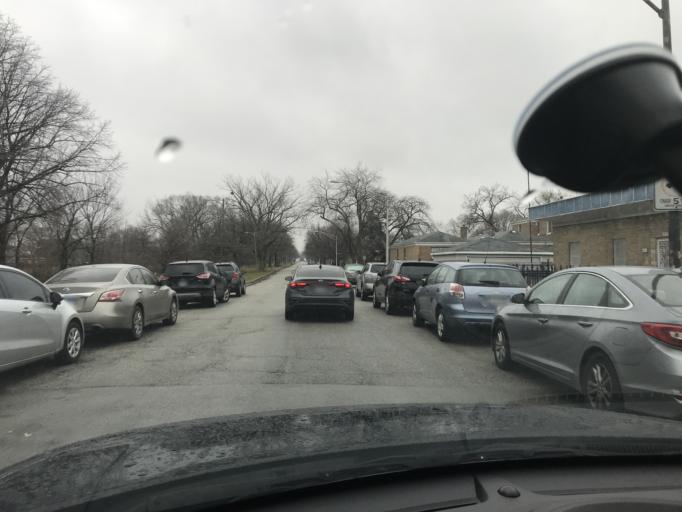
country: US
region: Illinois
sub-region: Cook County
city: Calumet Park
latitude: 41.7214
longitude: -87.6340
